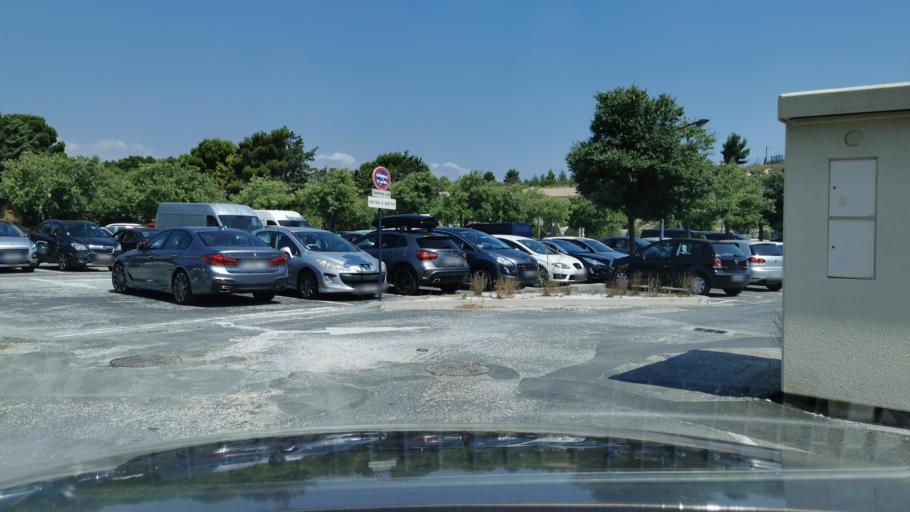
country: FR
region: Languedoc-Roussillon
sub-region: Departement de l'Aude
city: Leucate
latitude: 42.9111
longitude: 3.0243
